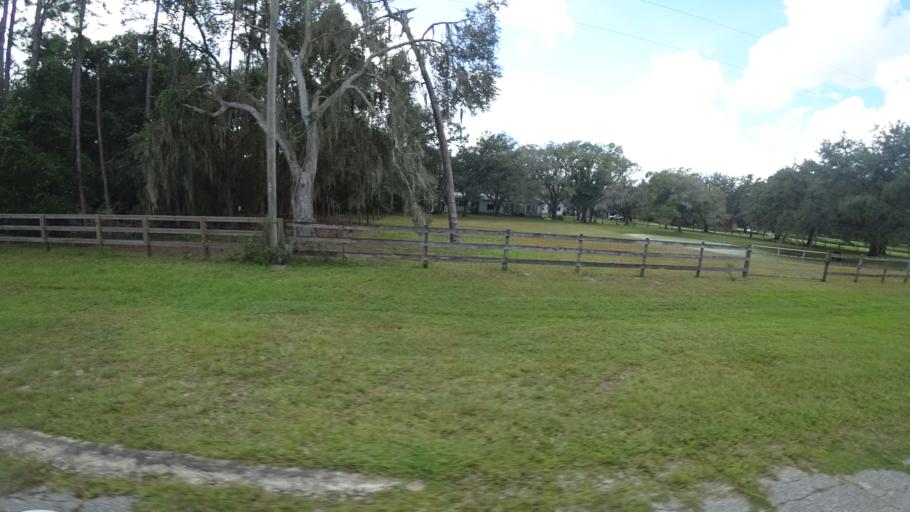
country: US
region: Florida
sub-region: Sarasota County
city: Lake Sarasota
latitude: 27.2799
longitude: -82.2272
